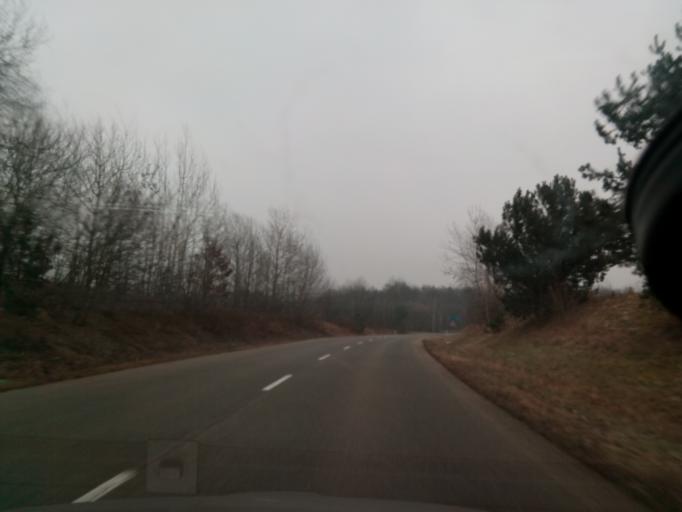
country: SK
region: Kosicky
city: Moldava nad Bodvou
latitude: 48.6913
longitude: 21.0526
